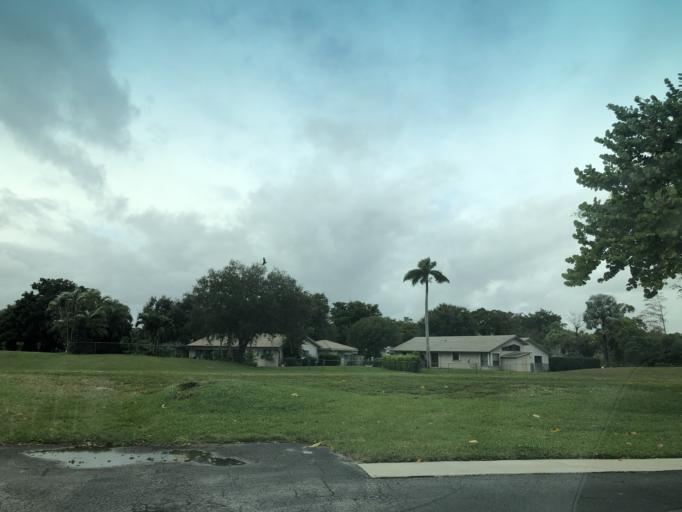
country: US
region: Florida
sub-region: Broward County
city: Margate
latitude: 26.2465
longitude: -80.2336
